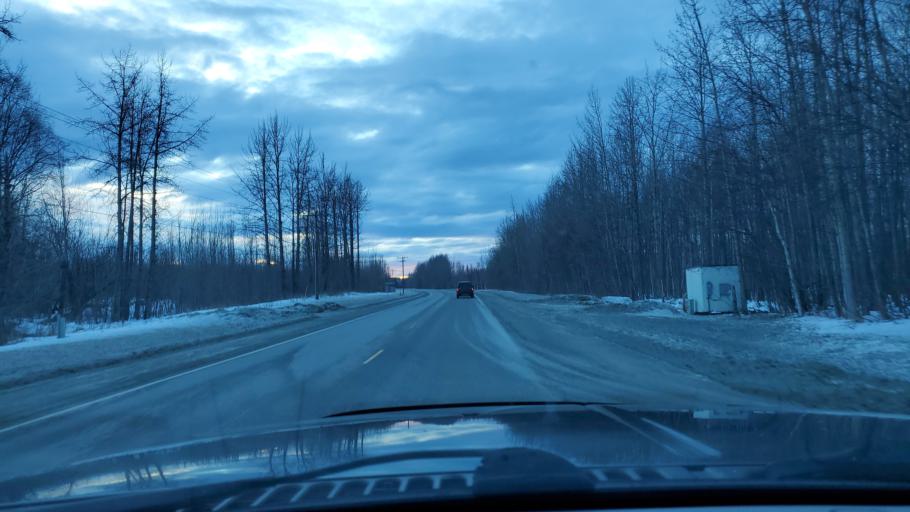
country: US
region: Alaska
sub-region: Matanuska-Susitna Borough
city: Farm Loop
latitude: 61.6635
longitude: -149.0876
